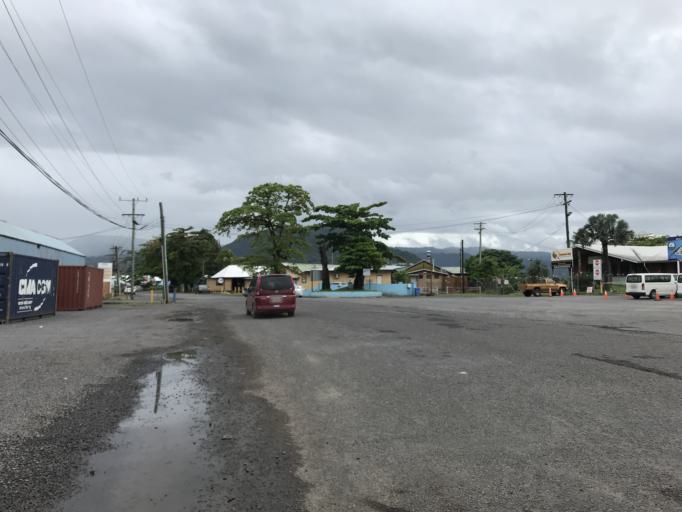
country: WS
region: Tuamasaga
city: Apia
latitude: -13.8265
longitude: -171.7586
